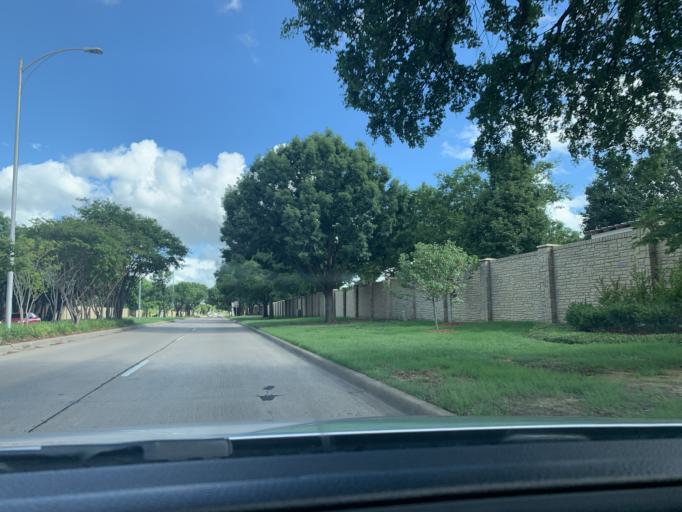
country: US
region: Texas
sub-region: Dallas County
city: Grand Prairie
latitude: 32.6679
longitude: -97.0438
